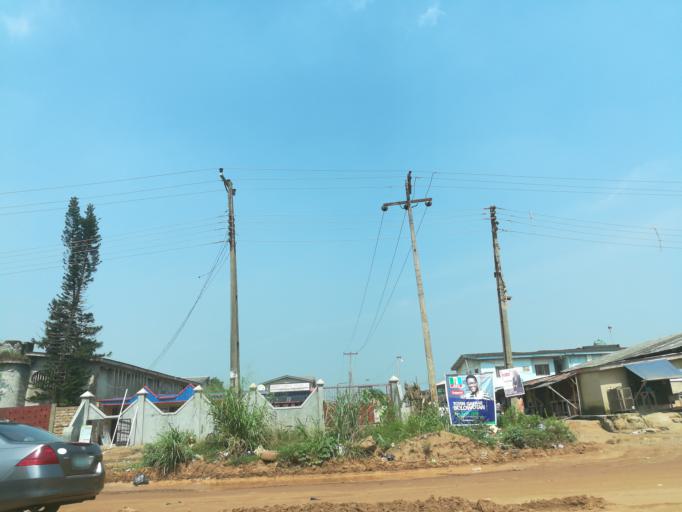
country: NG
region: Lagos
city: Ikorodu
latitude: 6.6532
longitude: 3.4763
